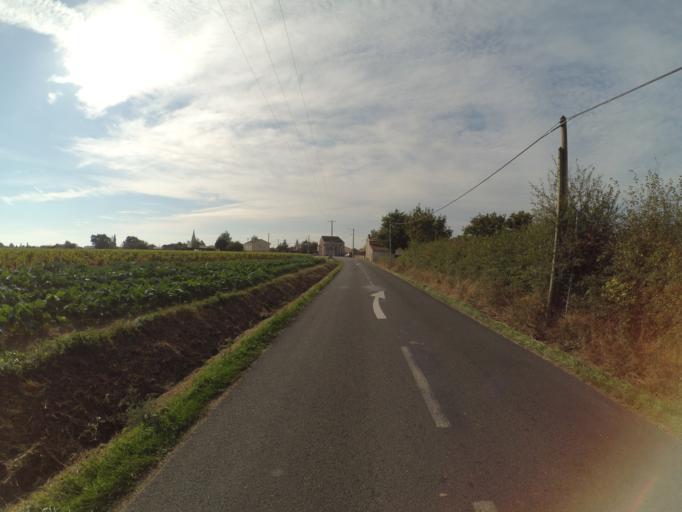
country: FR
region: Pays de la Loire
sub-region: Departement de Maine-et-Loire
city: Tillieres
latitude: 47.1491
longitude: -1.1658
